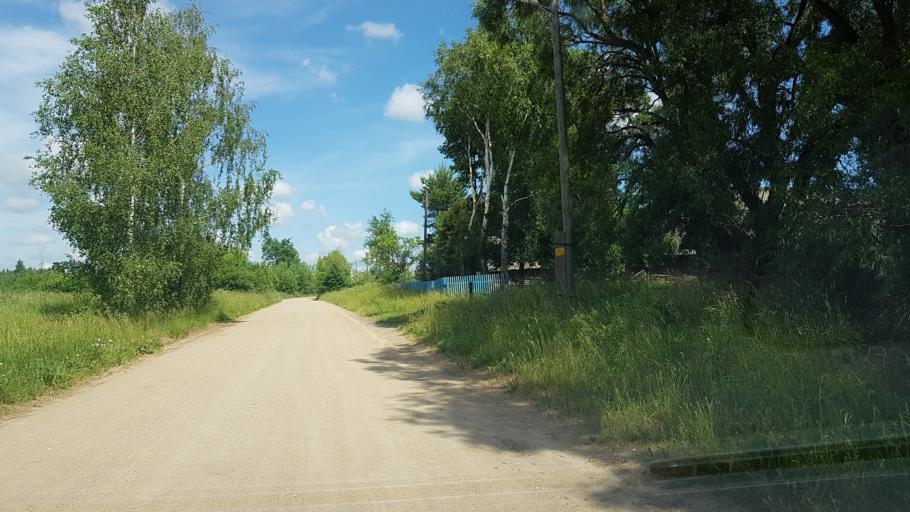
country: BY
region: Vitebsk
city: Dubrowna
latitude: 54.4875
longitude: 30.7962
